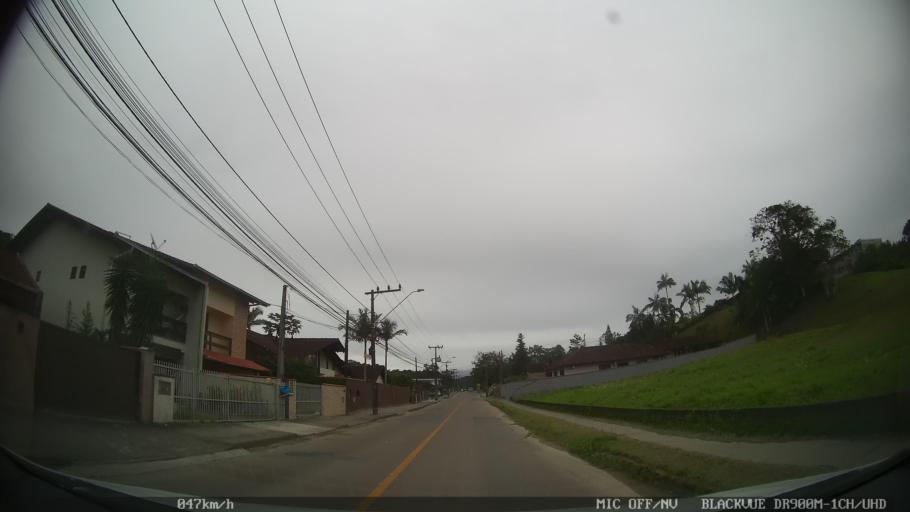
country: BR
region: Santa Catarina
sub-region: Joinville
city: Joinville
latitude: -26.2776
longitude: -48.9107
